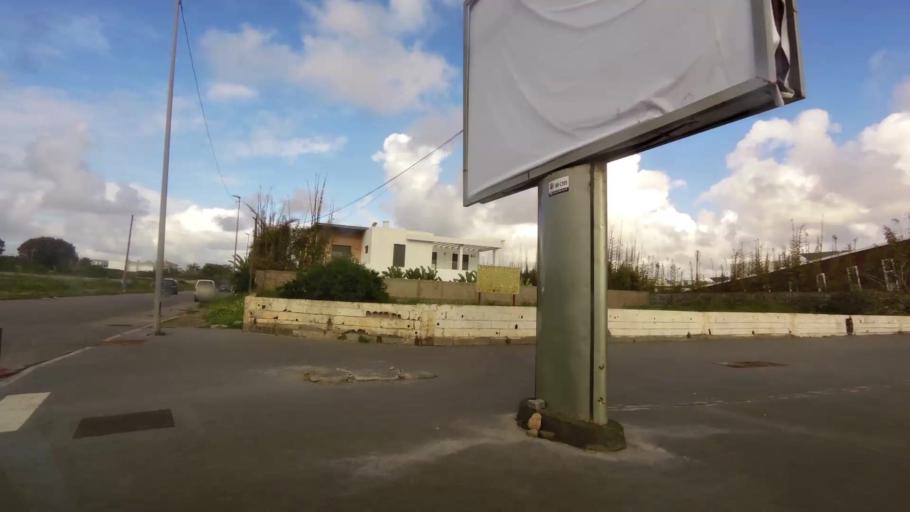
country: MA
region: Grand Casablanca
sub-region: Casablanca
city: Casablanca
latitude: 33.5754
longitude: -7.7013
